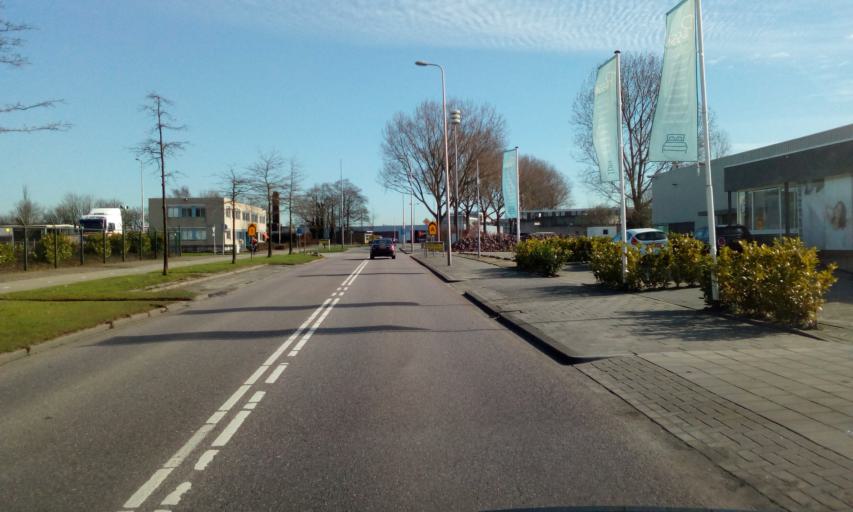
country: NL
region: South Holland
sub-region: Gemeente Alphen aan den Rijn
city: Alphen aan den Rijn
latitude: 52.1336
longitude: 4.6428
